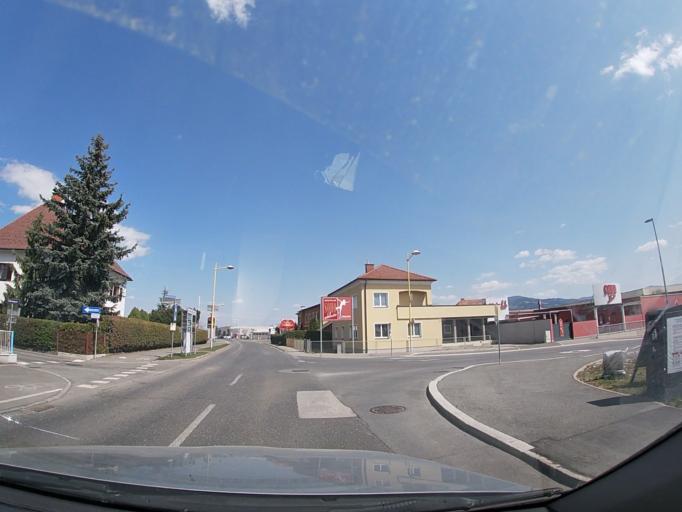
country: AT
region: Styria
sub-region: Politischer Bezirk Murtal
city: Zeltweg
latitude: 47.1923
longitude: 14.7581
